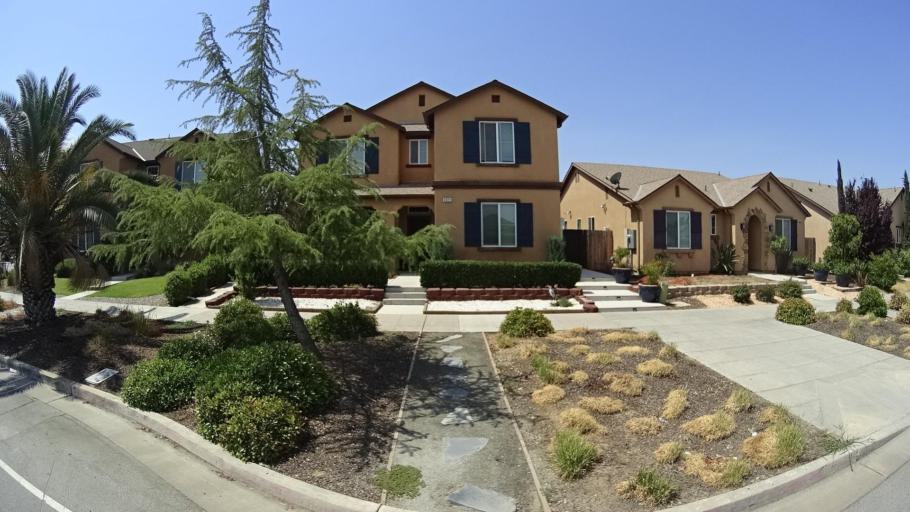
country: US
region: California
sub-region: Fresno County
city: Sunnyside
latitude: 36.7393
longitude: -119.6856
